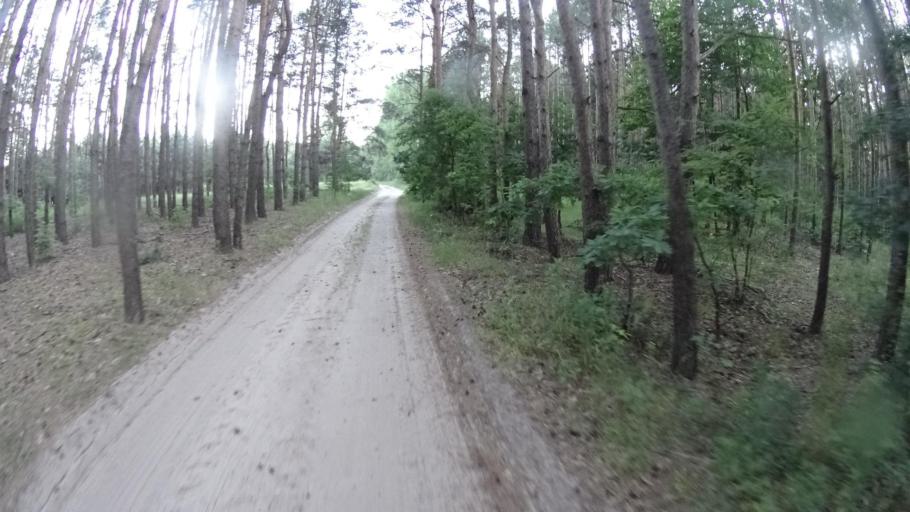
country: PL
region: Masovian Voivodeship
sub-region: Powiat warszawski zachodni
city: Jozefow
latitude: 52.2714
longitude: 20.6956
